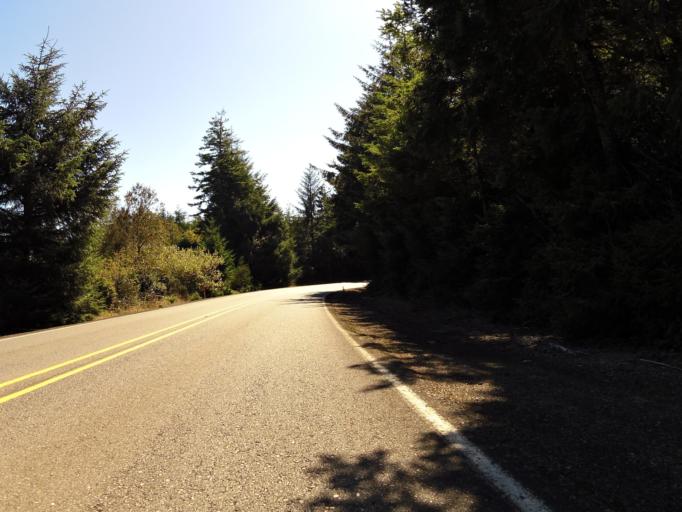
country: US
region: Oregon
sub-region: Coos County
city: Barview
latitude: 43.2434
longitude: -124.3331
